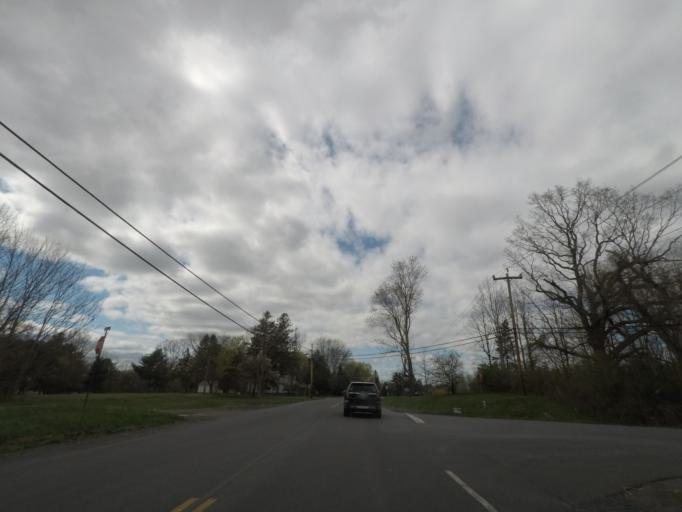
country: US
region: New York
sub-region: Columbia County
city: Chatham
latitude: 42.3669
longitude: -73.6190
